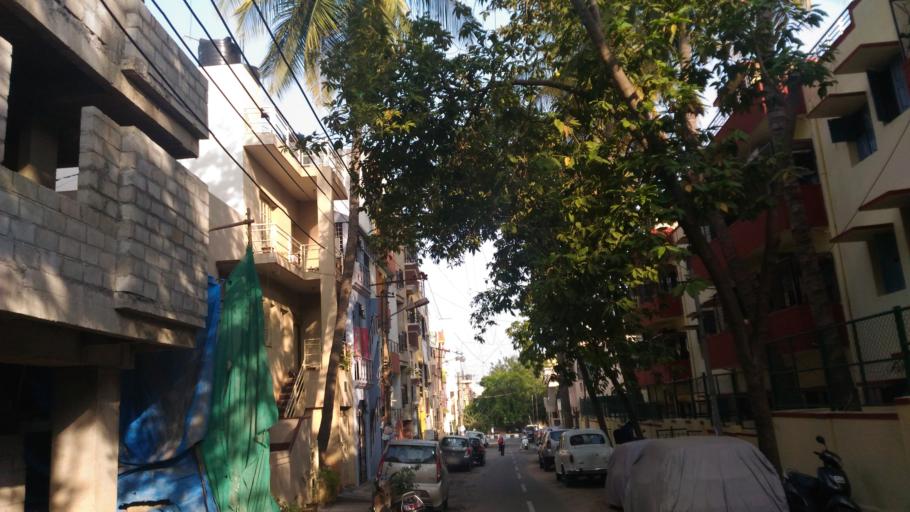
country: IN
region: Karnataka
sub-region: Bangalore Urban
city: Bangalore
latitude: 12.9225
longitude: 77.5960
